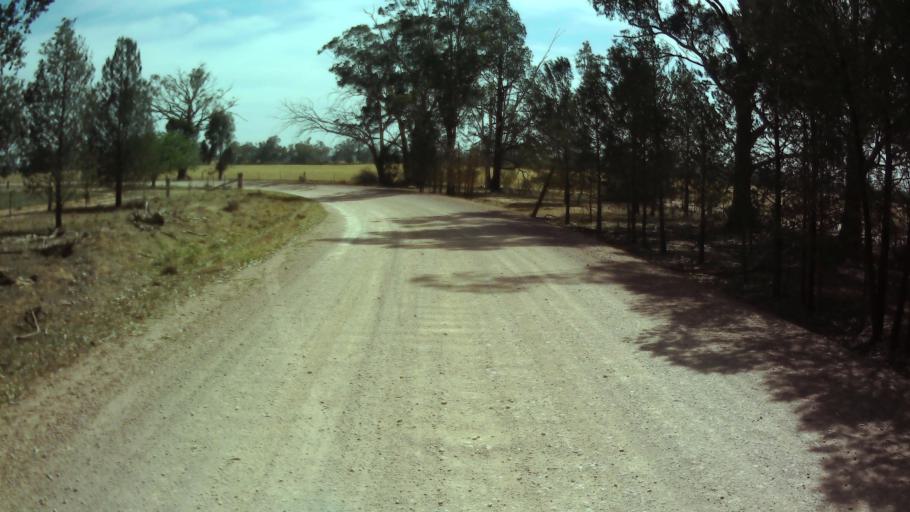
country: AU
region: New South Wales
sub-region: Weddin
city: Grenfell
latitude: -34.0366
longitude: 148.0817
